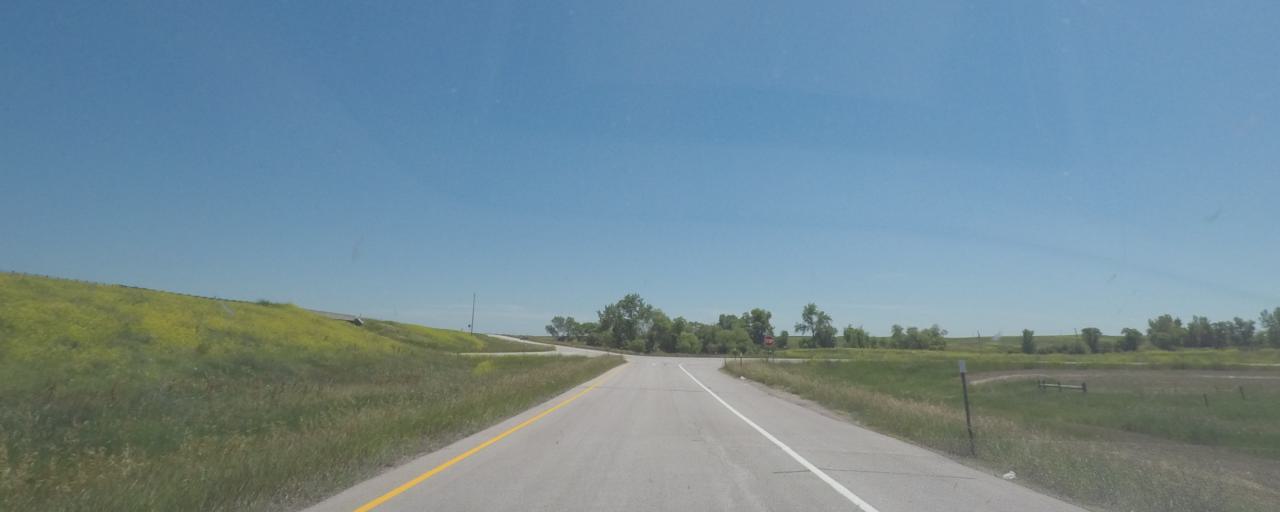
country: US
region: South Dakota
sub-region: Haakon County
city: Philip
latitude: 43.9373
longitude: -102.1535
